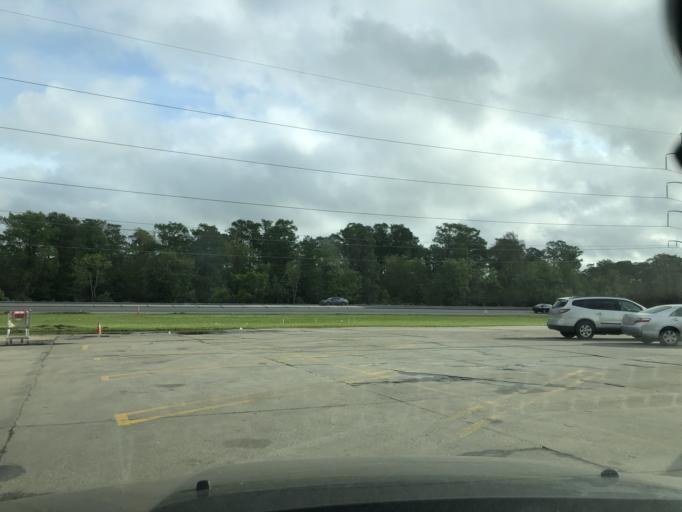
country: US
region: Louisiana
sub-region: Saint Charles Parish
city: New Sarpy
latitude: 29.9868
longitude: -90.3626
